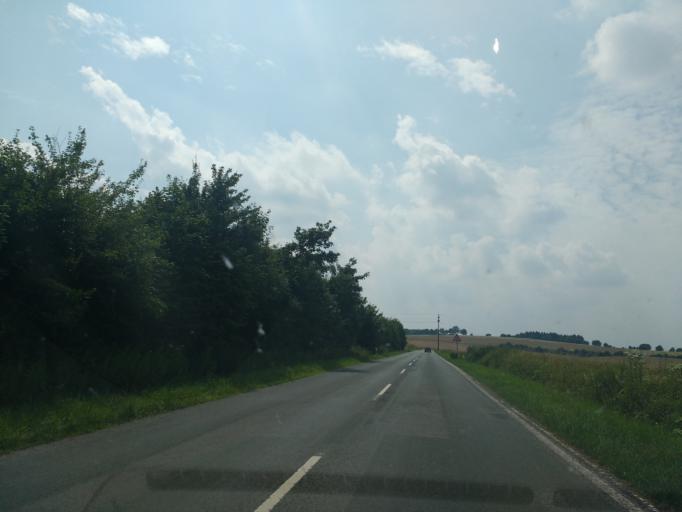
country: DE
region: North Rhine-Westphalia
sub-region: Regierungsbezirk Detmold
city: Dorentrup
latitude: 52.0749
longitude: 8.9737
